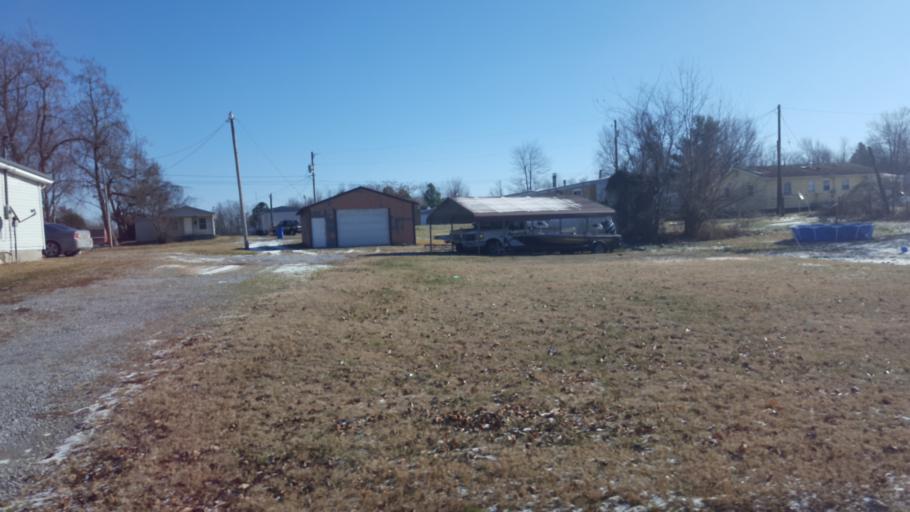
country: US
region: Kentucky
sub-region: Crittenden County
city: Marion
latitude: 37.3348
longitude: -88.0755
